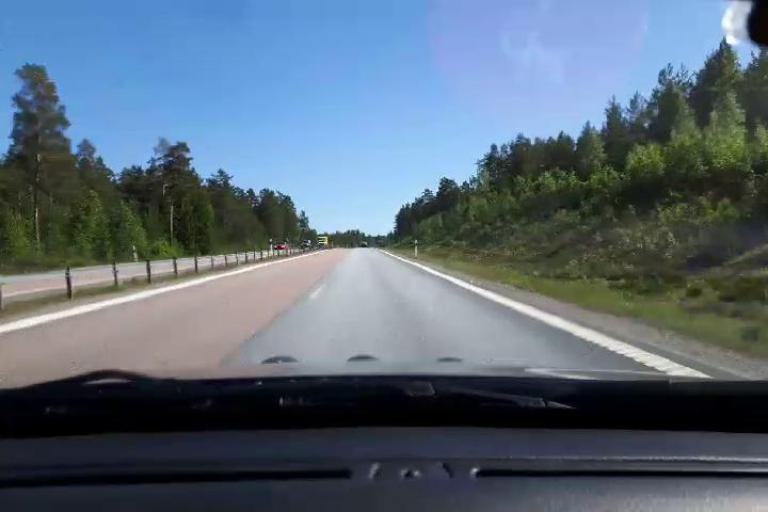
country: SE
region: Gaevleborg
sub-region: Soderhamns Kommun
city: Soderhamn
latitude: 61.3245
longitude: 17.0286
